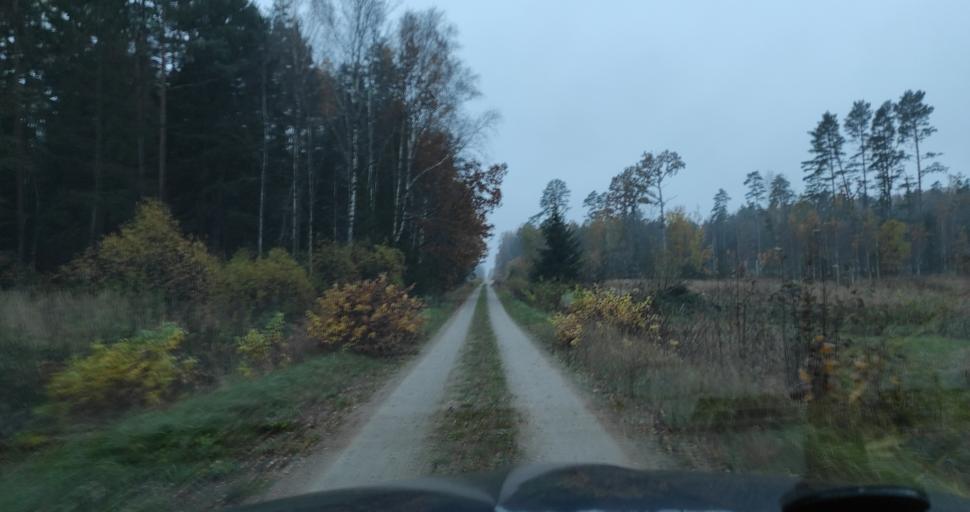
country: LV
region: Pavilostas
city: Pavilosta
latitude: 56.7475
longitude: 21.2848
